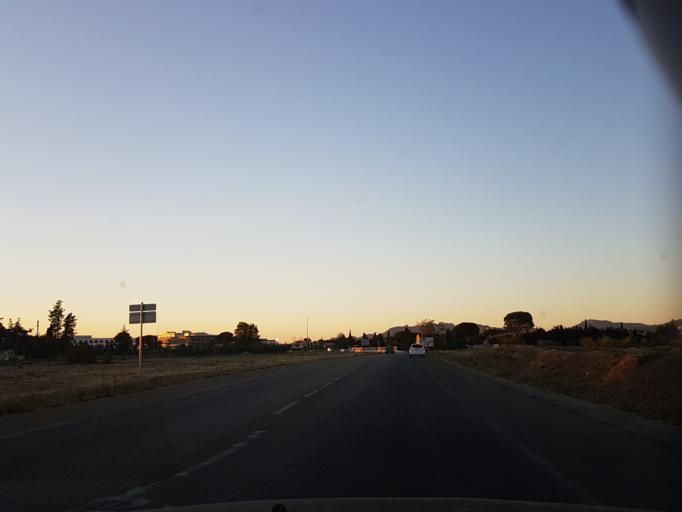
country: FR
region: Provence-Alpes-Cote d'Azur
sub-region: Departement du Vaucluse
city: Carpentras
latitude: 44.0423
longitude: 5.0303
